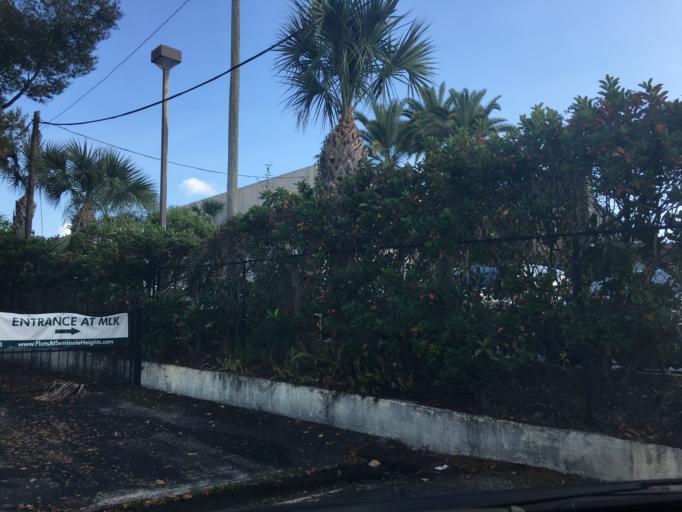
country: US
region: Florida
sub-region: Hillsborough County
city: Tampa
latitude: 27.9822
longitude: -82.4729
